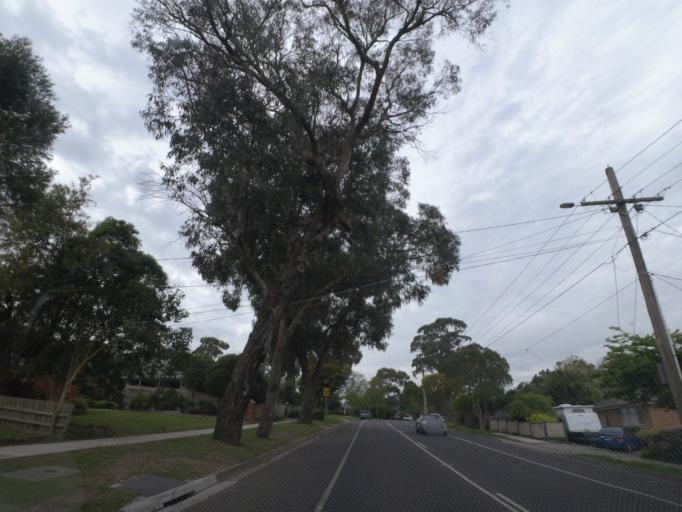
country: AU
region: Victoria
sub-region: Knox
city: The Basin
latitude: -37.8513
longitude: 145.3029
